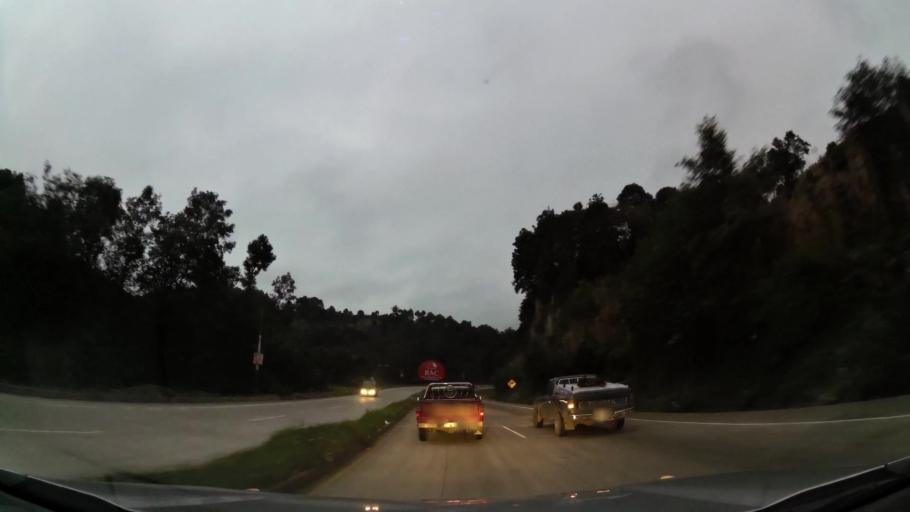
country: GT
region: Chimaltenango
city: Tecpan Guatemala
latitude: 14.8312
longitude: -91.0405
